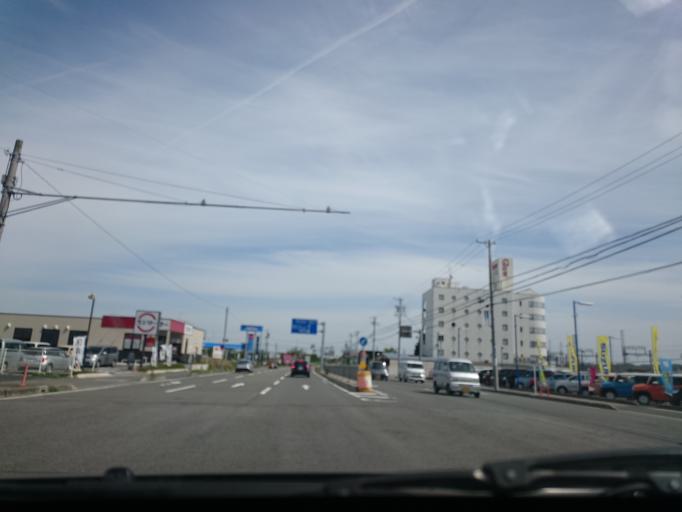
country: JP
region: Mie
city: Komono
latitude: 34.9880
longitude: 136.5522
